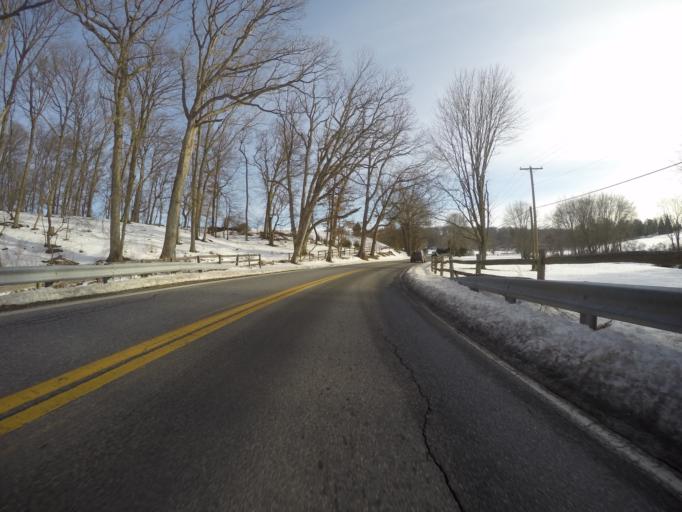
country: US
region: Maryland
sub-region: Harford County
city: Jarrettsville
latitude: 39.5387
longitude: -76.5478
